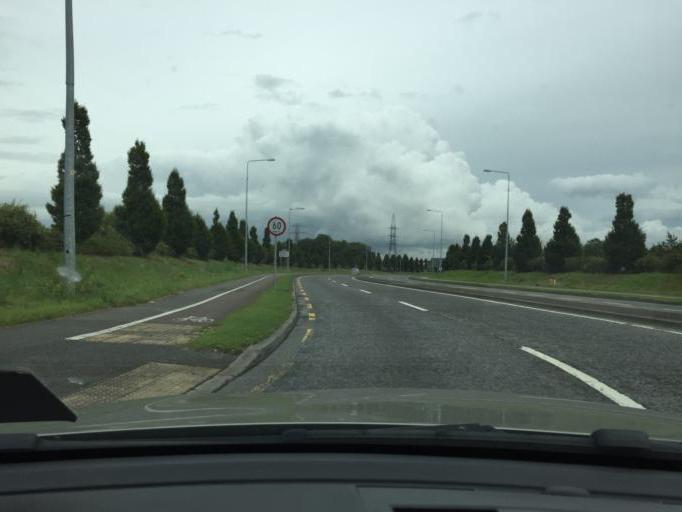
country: IE
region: Leinster
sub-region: Kildare
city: Celbridge
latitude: 53.3655
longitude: -6.5273
